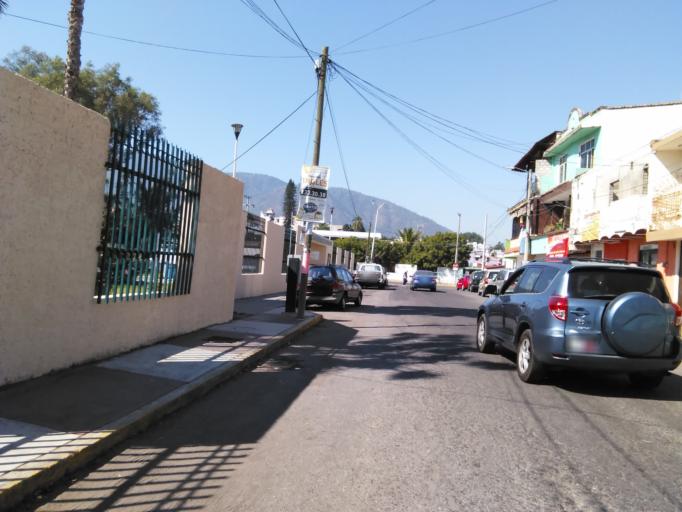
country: MX
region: Nayarit
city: Tepic
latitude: 21.4975
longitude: -104.8917
